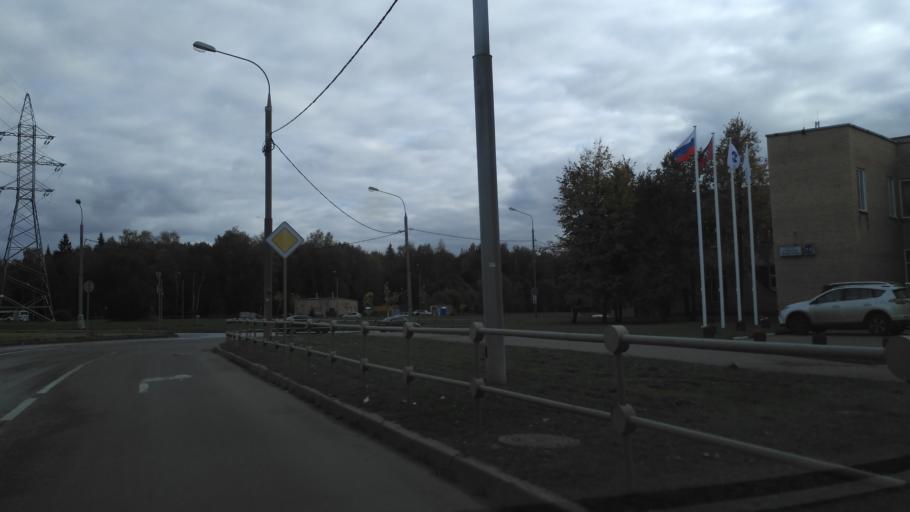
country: RU
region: Moskovskaya
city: Alabushevo
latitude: 56.0083
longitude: 37.1661
